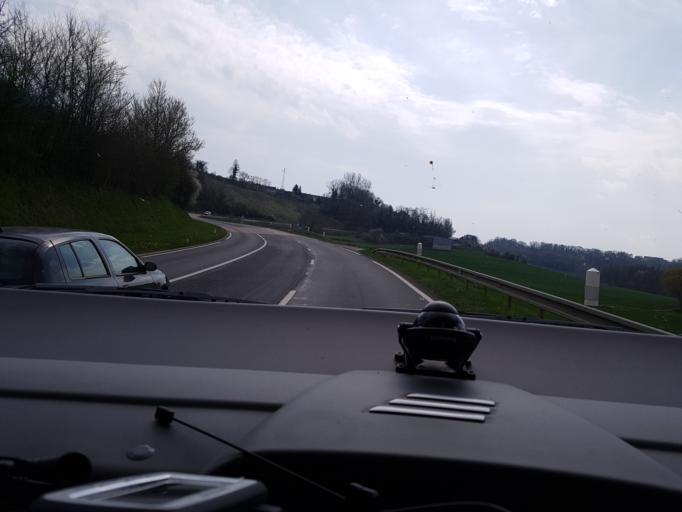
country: FR
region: Picardie
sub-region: Departement de l'Aisne
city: Coucy-le-Chateau-Auffrique
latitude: 49.4826
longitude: 3.3399
